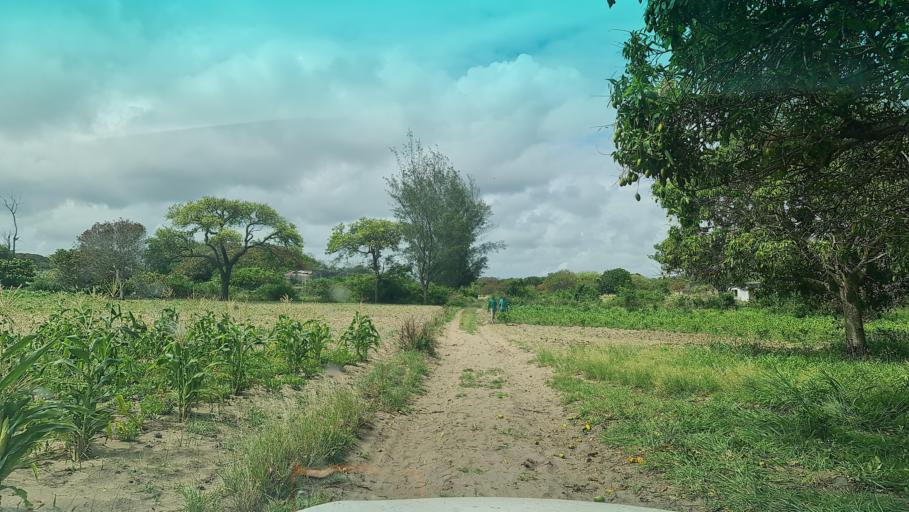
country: MZ
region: Maputo
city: Manhica
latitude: -25.3972
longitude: 33.0279
